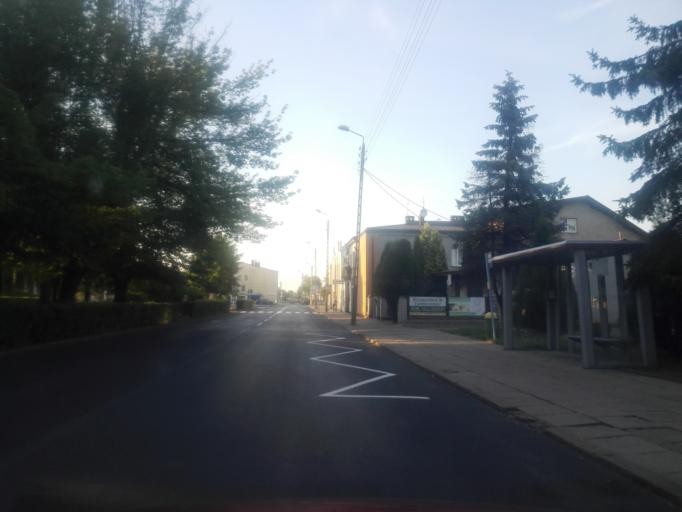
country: PL
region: Lodz Voivodeship
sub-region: Powiat wielunski
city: Wielun
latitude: 51.2207
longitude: 18.5741
